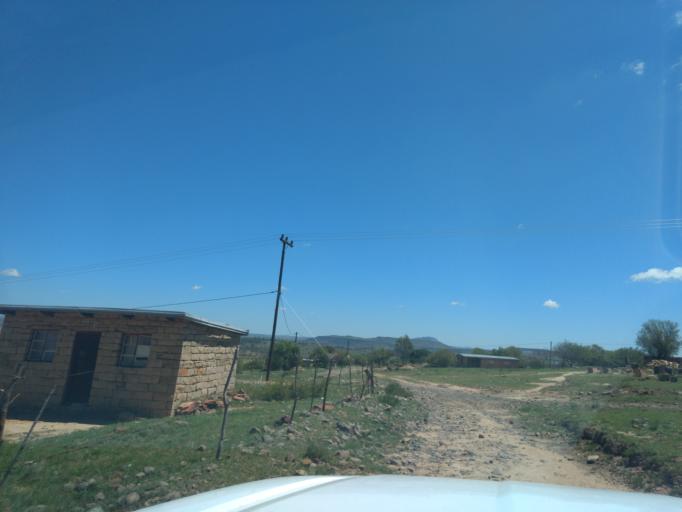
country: LS
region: Maseru
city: Maseru
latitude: -29.4575
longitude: 27.3737
